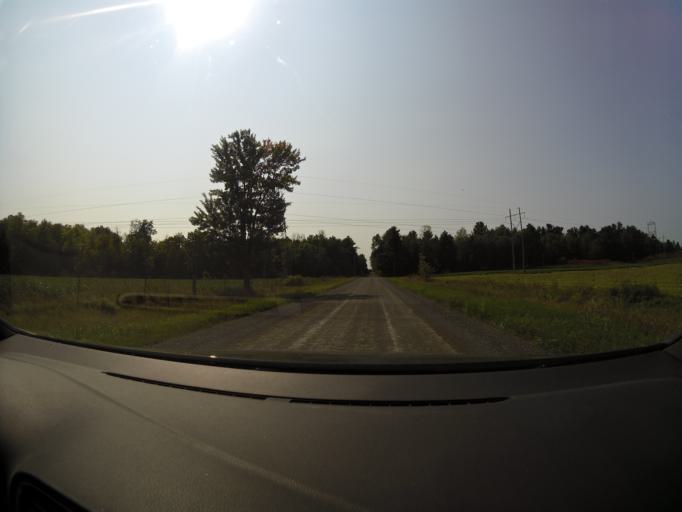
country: CA
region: Ontario
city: Arnprior
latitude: 45.4417
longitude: -76.1676
